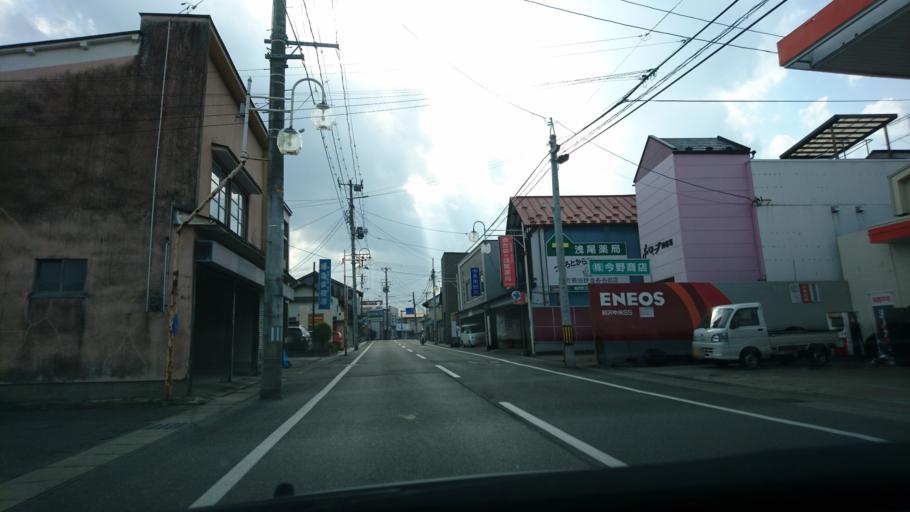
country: JP
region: Iwate
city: Mizusawa
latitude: 39.0475
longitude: 141.1225
